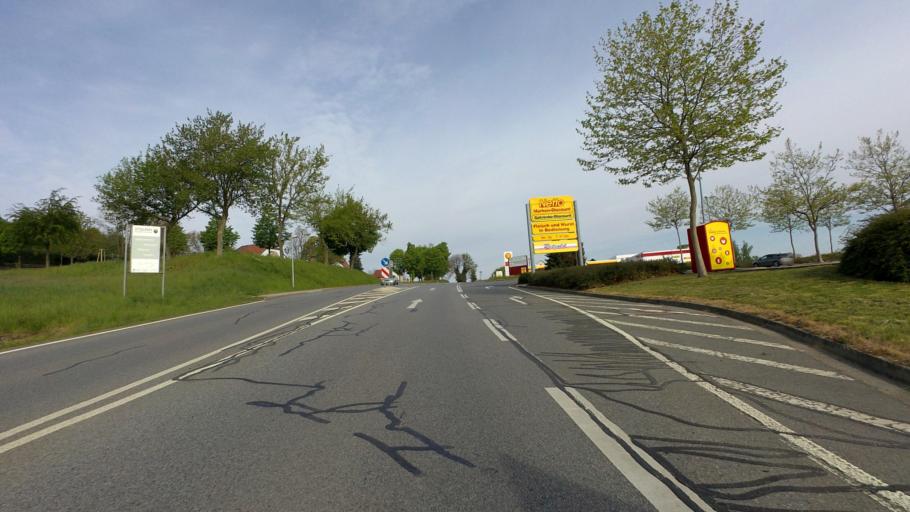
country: DE
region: Saxony
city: Stolpen
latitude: 51.0501
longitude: 14.0890
